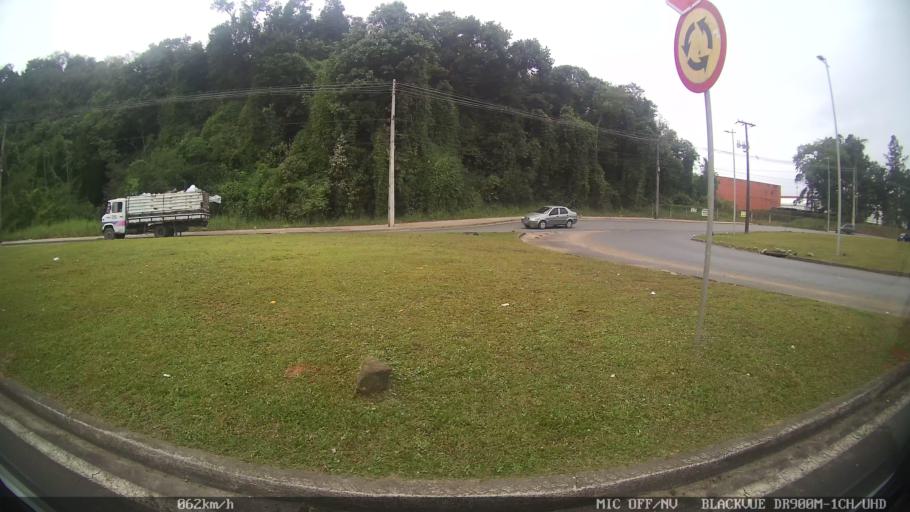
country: BR
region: Santa Catarina
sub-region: Joinville
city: Joinville
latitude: -26.2476
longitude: -48.8430
